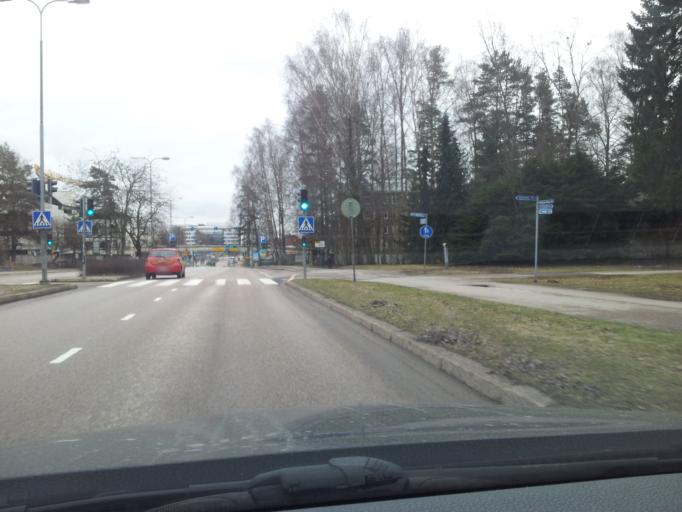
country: FI
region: Uusimaa
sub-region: Helsinki
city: Otaniemi
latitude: 60.1765
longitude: 24.7998
